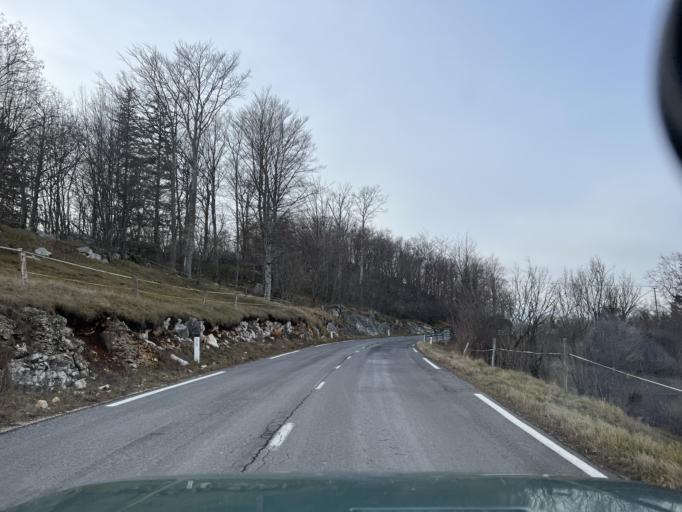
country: SI
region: Nova Gorica
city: Sempas
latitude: 45.9784
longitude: 13.7492
